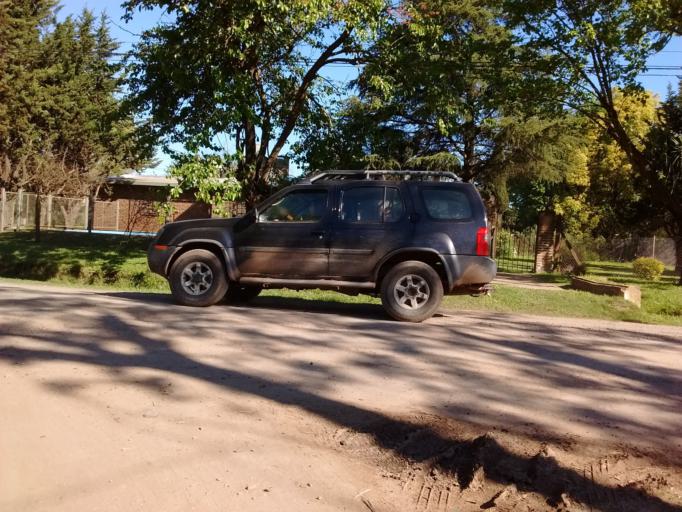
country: AR
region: Santa Fe
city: Funes
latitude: -32.9198
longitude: -60.8437
